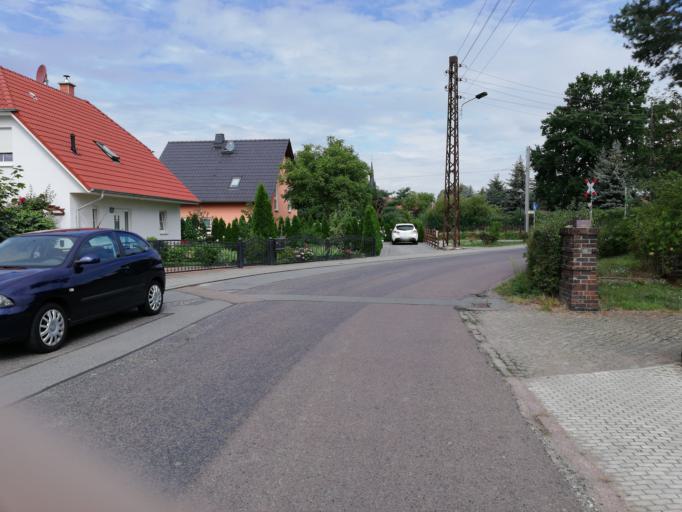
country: DE
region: Saxony
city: Weinbohla
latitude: 51.1586
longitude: 13.5664
